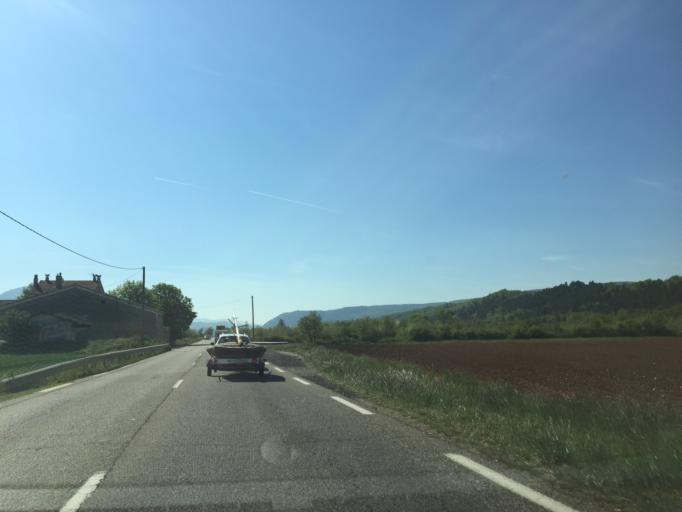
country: FR
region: Provence-Alpes-Cote d'Azur
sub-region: Departement des Alpes-de-Haute-Provence
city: Sisteron
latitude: 44.2395
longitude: 5.8965
